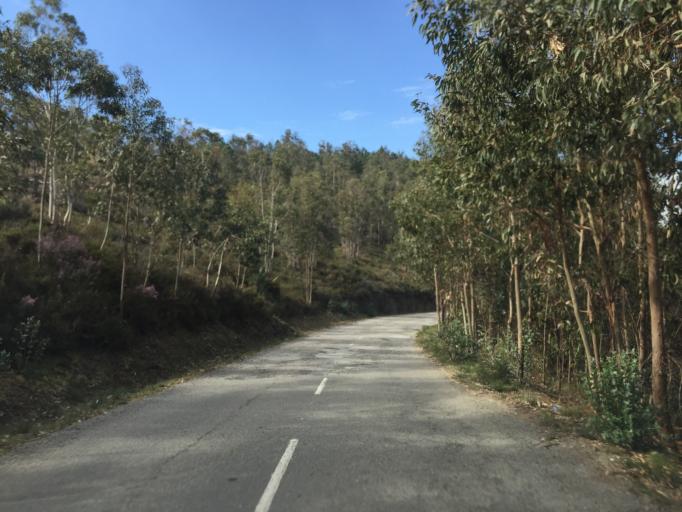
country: PT
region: Aveiro
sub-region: Arouca
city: Arouca
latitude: 40.9809
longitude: -8.2486
